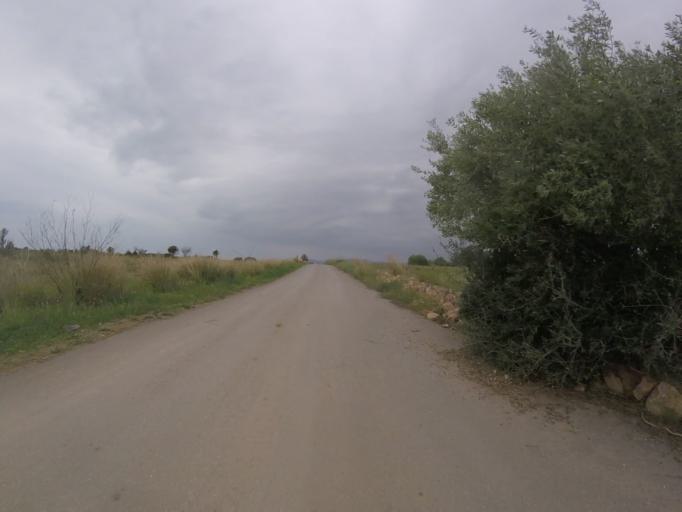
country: ES
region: Valencia
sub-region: Provincia de Castello
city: Torreblanca
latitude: 40.2139
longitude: 0.2462
